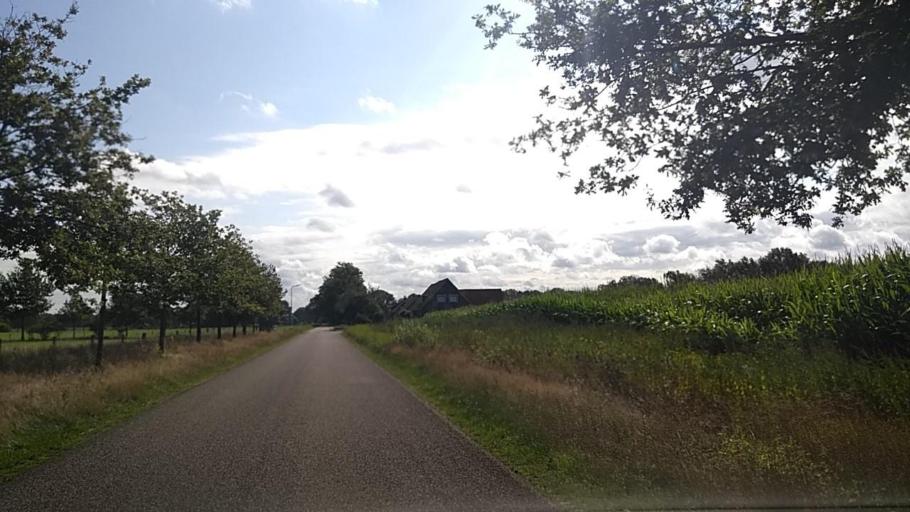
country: DE
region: Lower Saxony
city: Nordhorn
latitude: 52.3693
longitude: 7.0260
